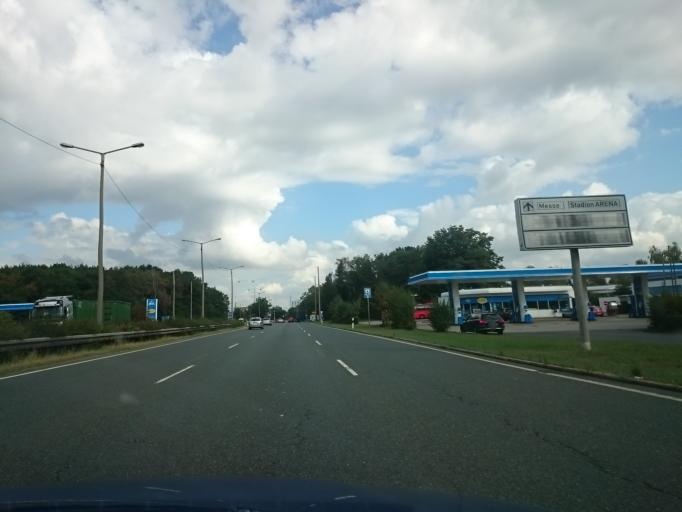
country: DE
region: Bavaria
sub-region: Regierungsbezirk Mittelfranken
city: Wendelstein
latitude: 49.4010
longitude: 11.1156
